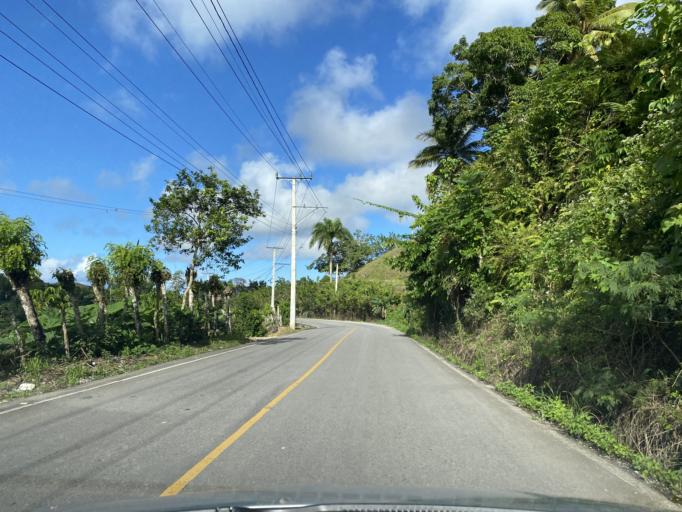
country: DO
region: Samana
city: Las Terrenas
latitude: 19.2632
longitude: -69.5658
